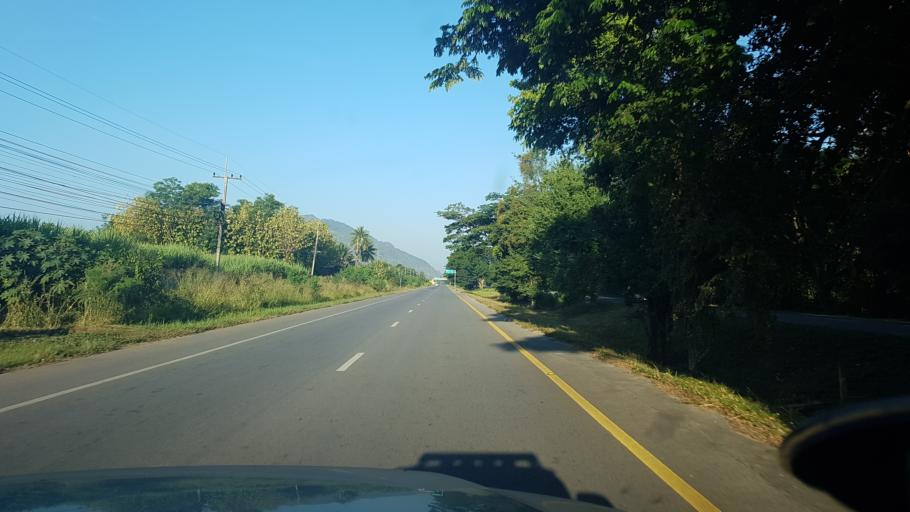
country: TH
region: Chaiyaphum
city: Khon San
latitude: 16.5982
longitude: 101.9079
